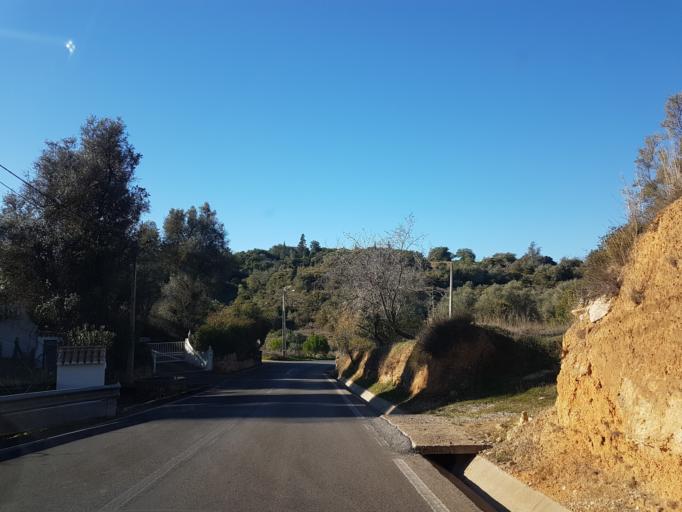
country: PT
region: Faro
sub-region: Lagoa
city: Lagoa
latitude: 37.1160
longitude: -8.4085
